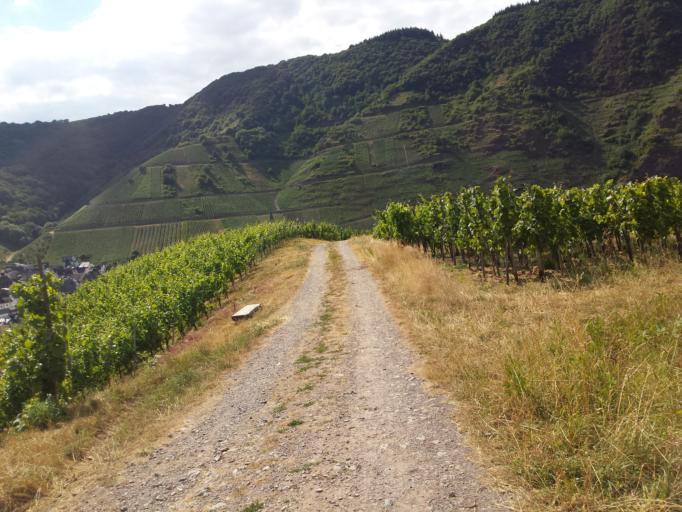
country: DE
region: Rheinland-Pfalz
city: Bremm
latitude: 50.1010
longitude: 7.1239
